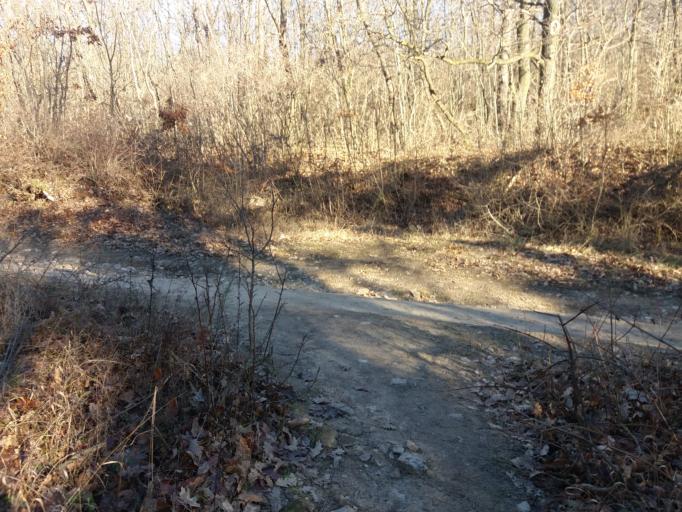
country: HU
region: Pest
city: Budaors
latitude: 47.4757
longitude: 18.9456
